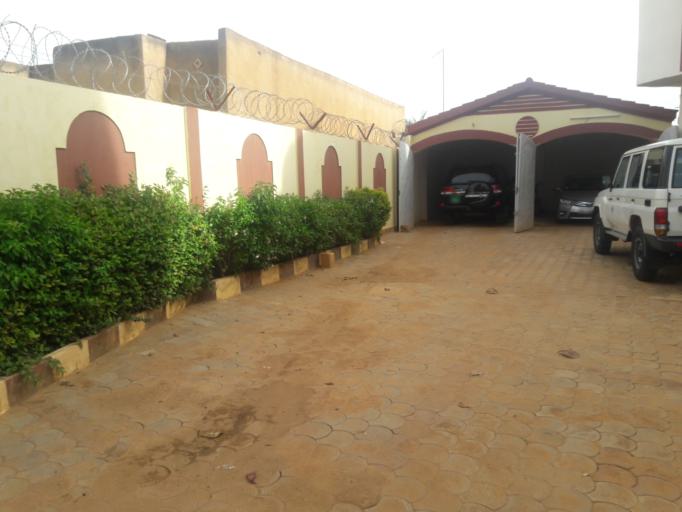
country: NE
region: Niamey
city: Niamey
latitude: 13.5400
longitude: 2.0642
